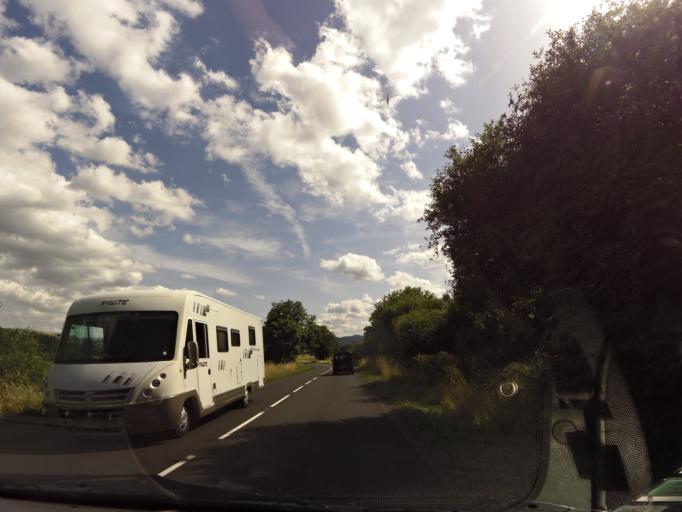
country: FR
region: Auvergne
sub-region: Departement du Puy-de-Dome
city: Aydat
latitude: 45.5324
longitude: 2.9466
